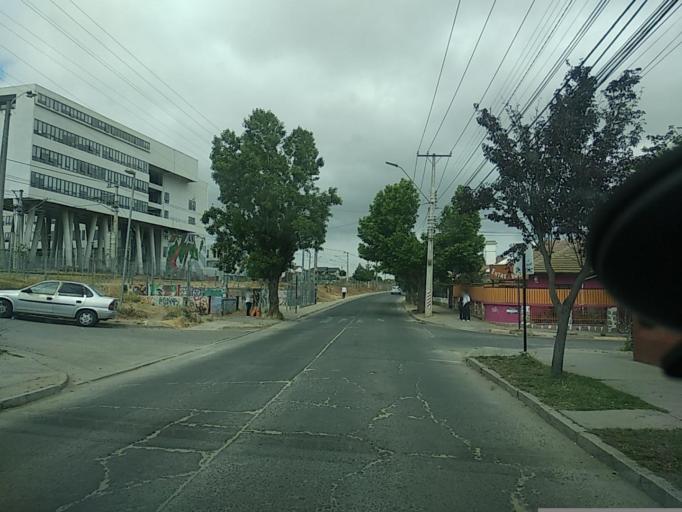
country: CL
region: Valparaiso
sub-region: Provincia de Marga Marga
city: Villa Alemana
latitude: -33.0421
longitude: -71.3747
